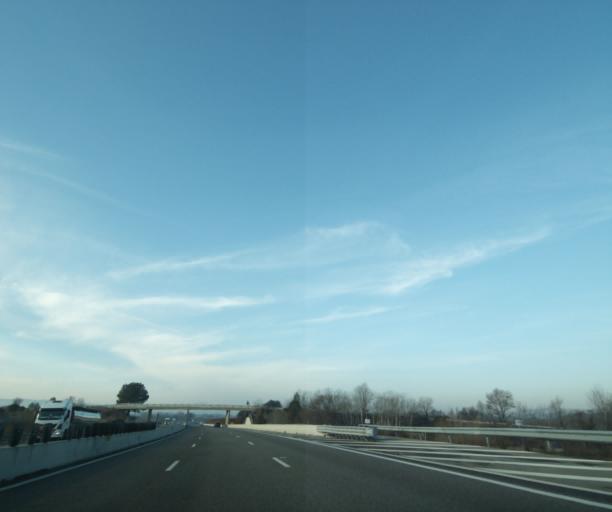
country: FR
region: Provence-Alpes-Cote d'Azur
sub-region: Departement des Bouches-du-Rhone
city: Trets
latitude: 43.4764
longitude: 5.7056
